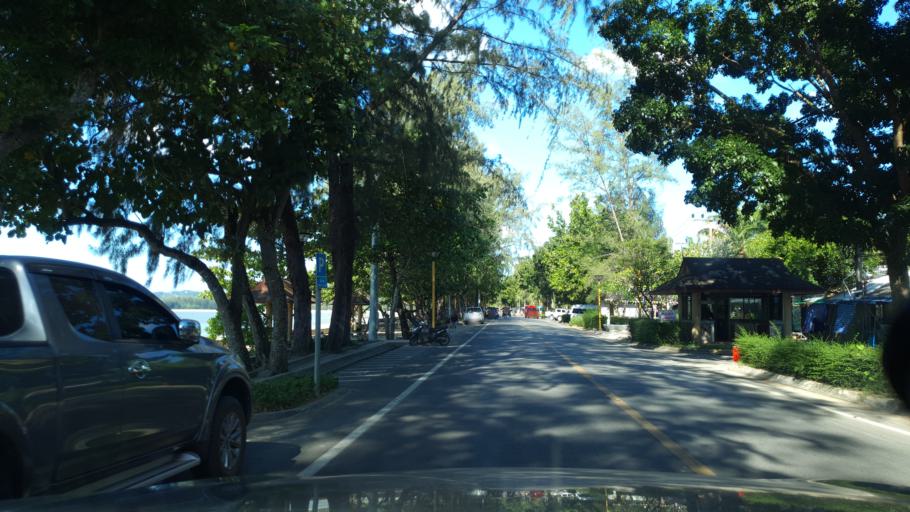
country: TH
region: Phangnga
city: Ban Ao Nang
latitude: 8.0434
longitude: 98.8091
